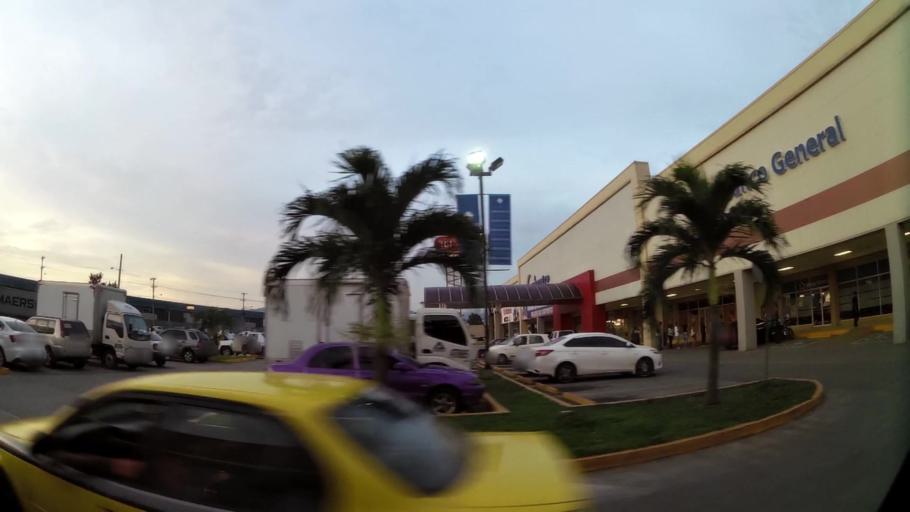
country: PA
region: Panama
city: Tocumen
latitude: 9.0772
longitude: -79.4004
